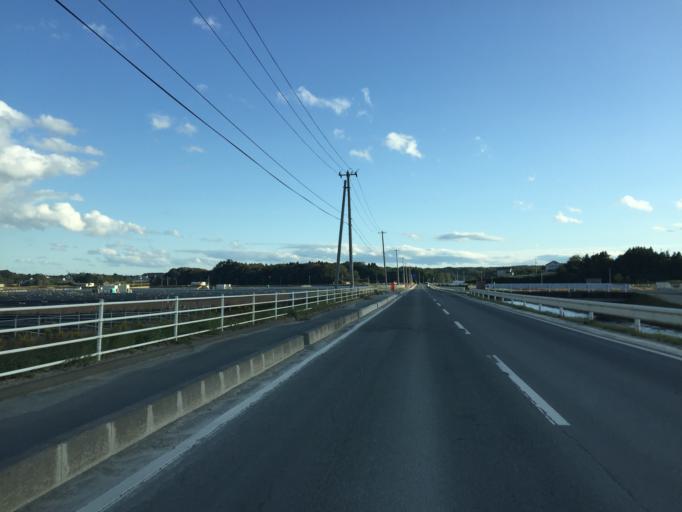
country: JP
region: Miyagi
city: Marumori
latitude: 37.7721
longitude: 140.9814
